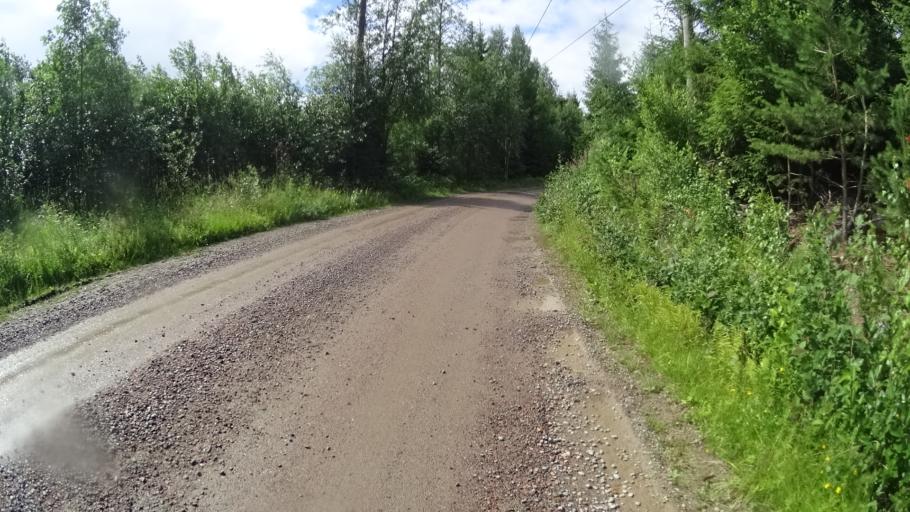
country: FI
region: Uusimaa
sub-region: Helsinki
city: Karkkila
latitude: 60.5856
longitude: 24.3200
